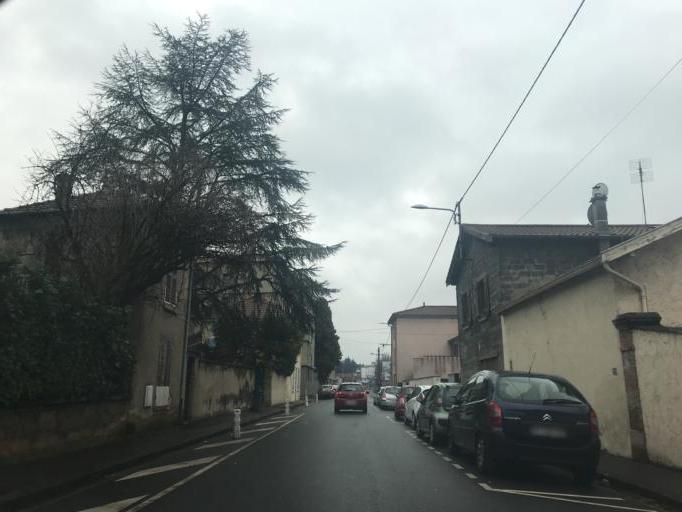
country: FR
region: Rhone-Alpes
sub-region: Departement du Rhone
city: Albigny-sur-Saone
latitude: 45.8738
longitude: 4.8391
